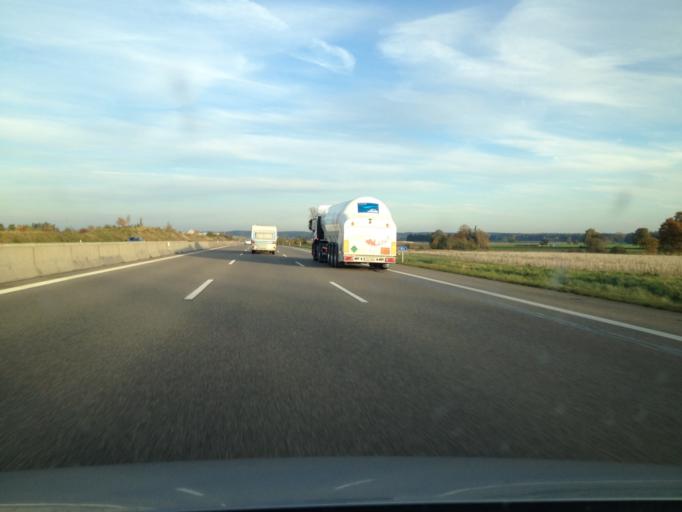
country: DE
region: Bavaria
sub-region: Swabia
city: Bubesheim
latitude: 48.4291
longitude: 10.2415
